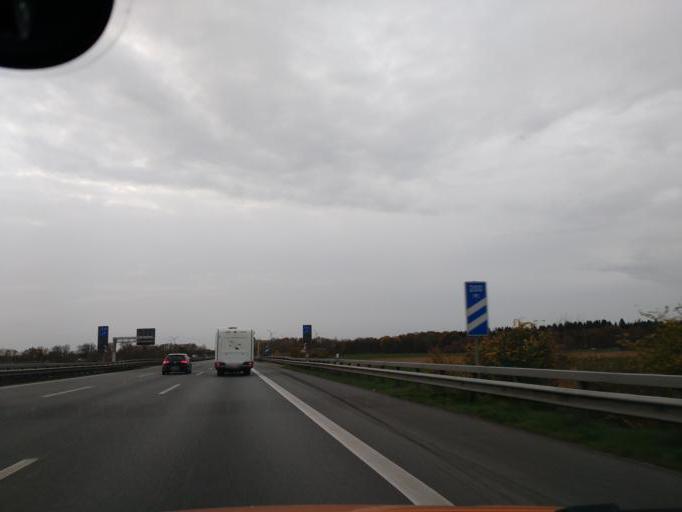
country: DE
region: Lower Saxony
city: Ottersberg
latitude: 53.0839
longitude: 9.1660
